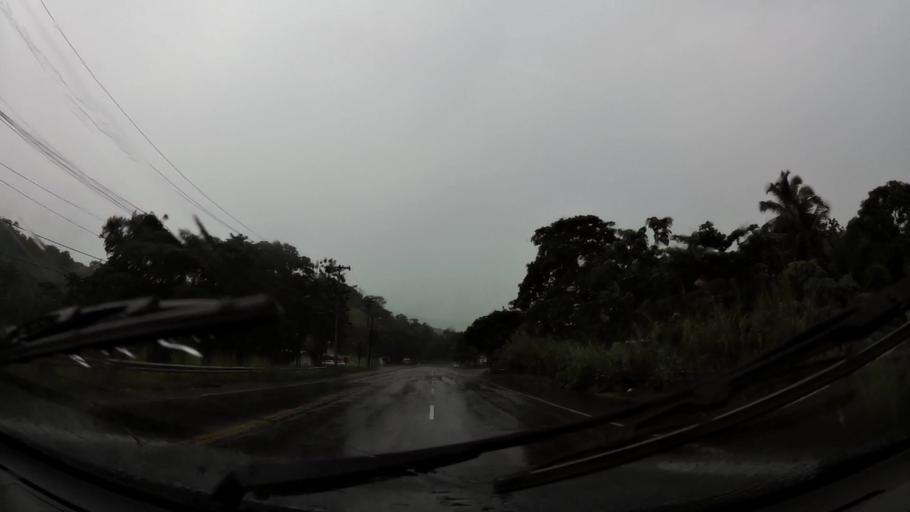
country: PA
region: Colon
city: Gatun
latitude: 9.2956
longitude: -79.7757
